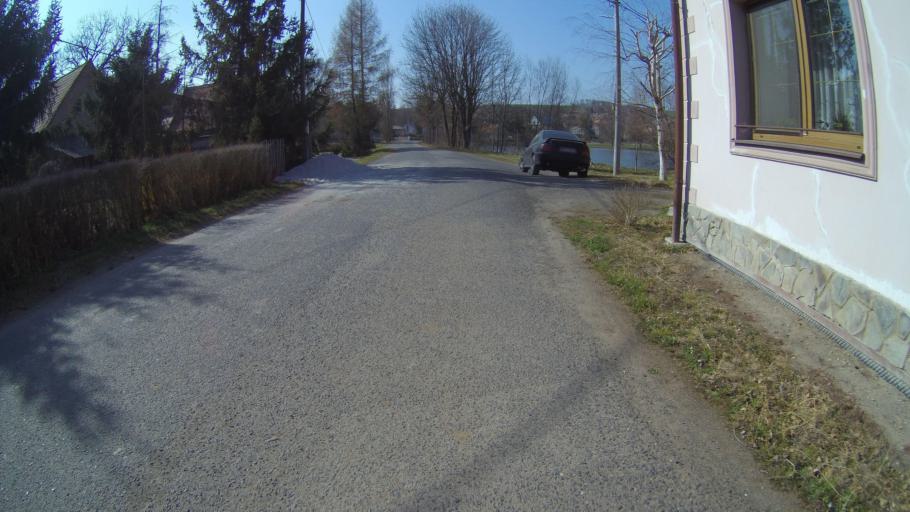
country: CZ
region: Ustecky
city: Mecholupy
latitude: 50.2511
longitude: 13.5196
